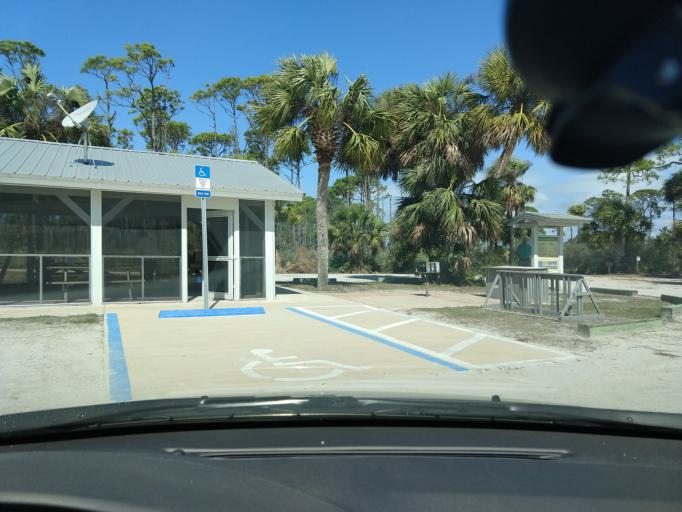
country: US
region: Florida
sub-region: Gulf County
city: Port Saint Joe
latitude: 29.7763
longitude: -85.4025
